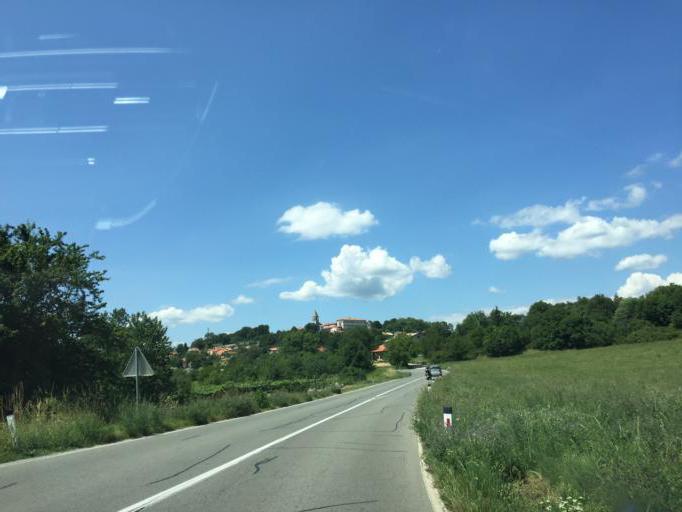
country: SI
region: Sezana
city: Sezana
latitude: 45.7511
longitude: 13.8598
